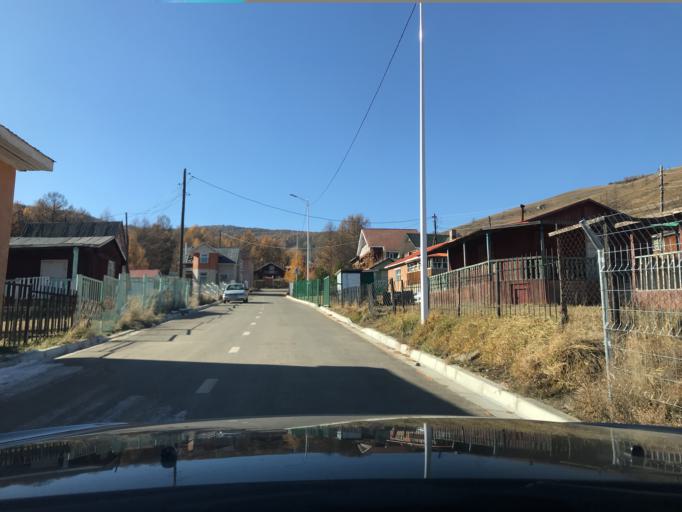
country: MN
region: Ulaanbaatar
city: Ulaanbaatar
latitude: 48.0383
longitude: 106.8908
